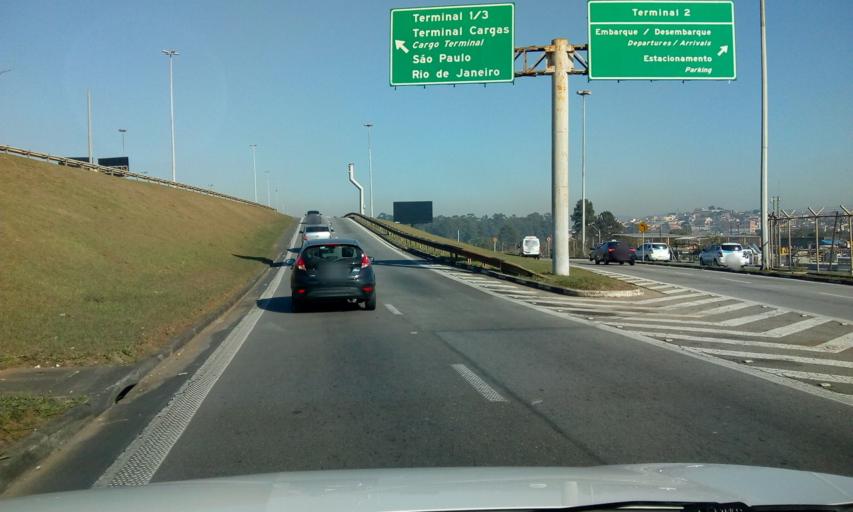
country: BR
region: Sao Paulo
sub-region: Guarulhos
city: Guarulhos
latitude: -23.4219
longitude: -46.4827
